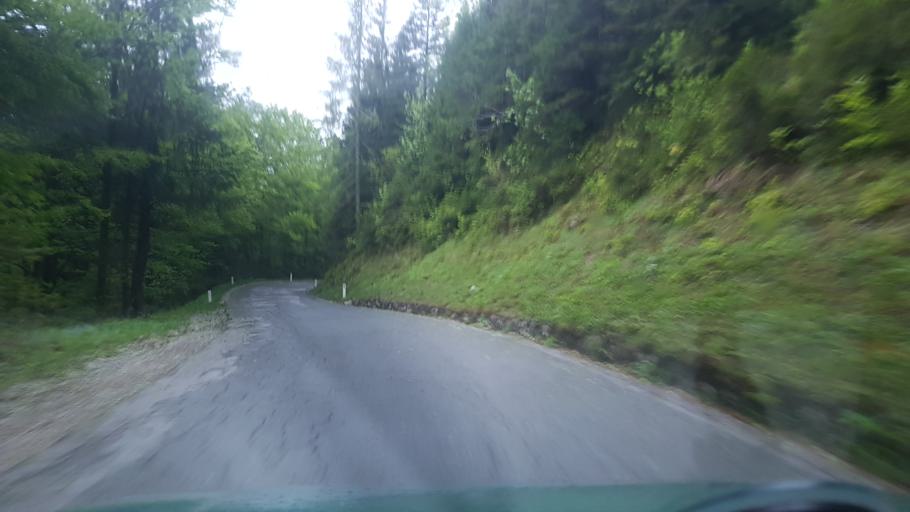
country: SI
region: Bohinj
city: Bohinjska Bistrica
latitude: 46.2300
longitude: 14.0227
